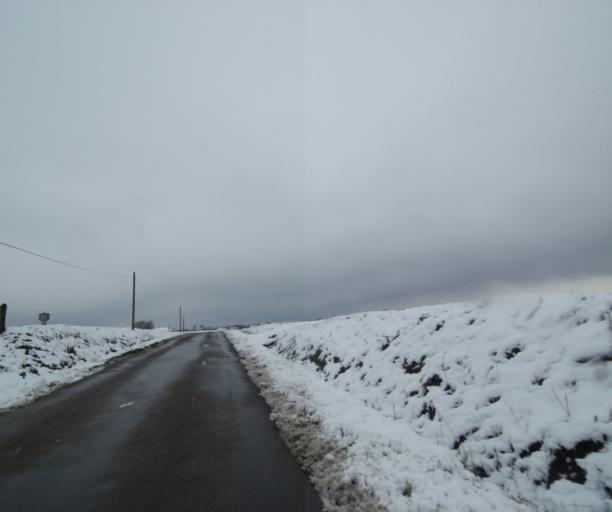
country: FR
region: Champagne-Ardenne
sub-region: Departement de la Haute-Marne
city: Laneuville-a-Remy
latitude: 48.5078
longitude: 4.8503
